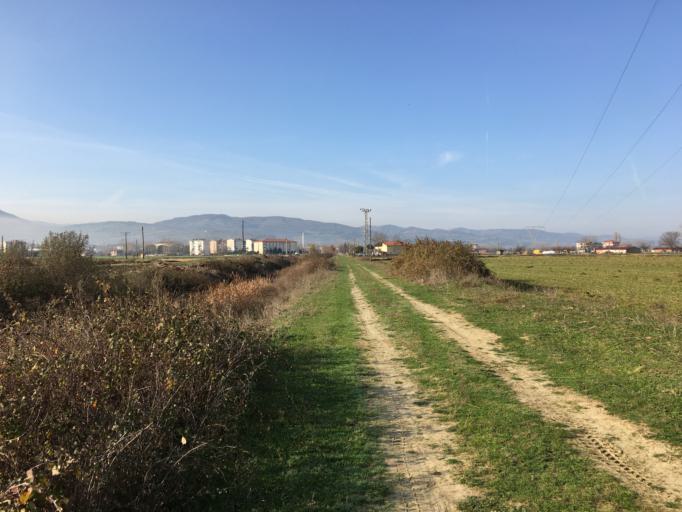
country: TR
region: Samsun
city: Alacam
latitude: 41.6224
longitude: 35.6229
